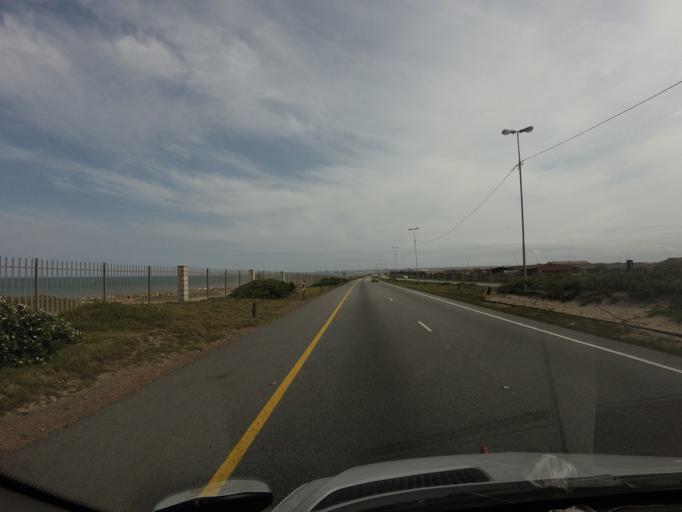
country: ZA
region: Eastern Cape
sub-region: Nelson Mandela Bay Metropolitan Municipality
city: Port Elizabeth
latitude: -33.8895
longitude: 25.6226
